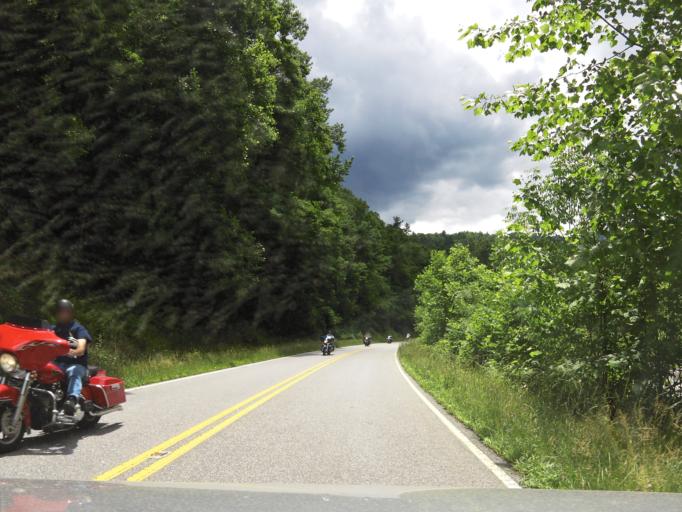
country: US
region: North Carolina
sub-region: Graham County
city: Robbinsville
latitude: 35.4295
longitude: -83.9063
